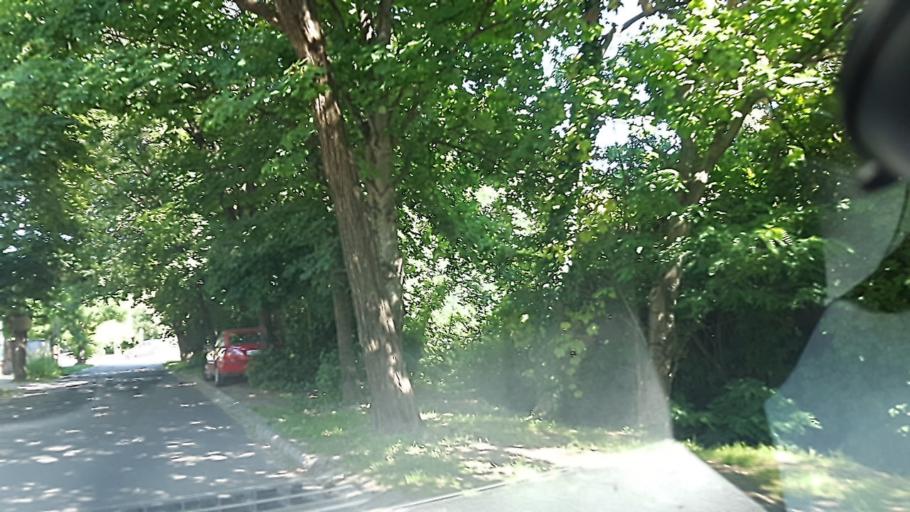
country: HU
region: Pest
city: Pilisszentivan
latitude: 47.6084
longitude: 18.9030
